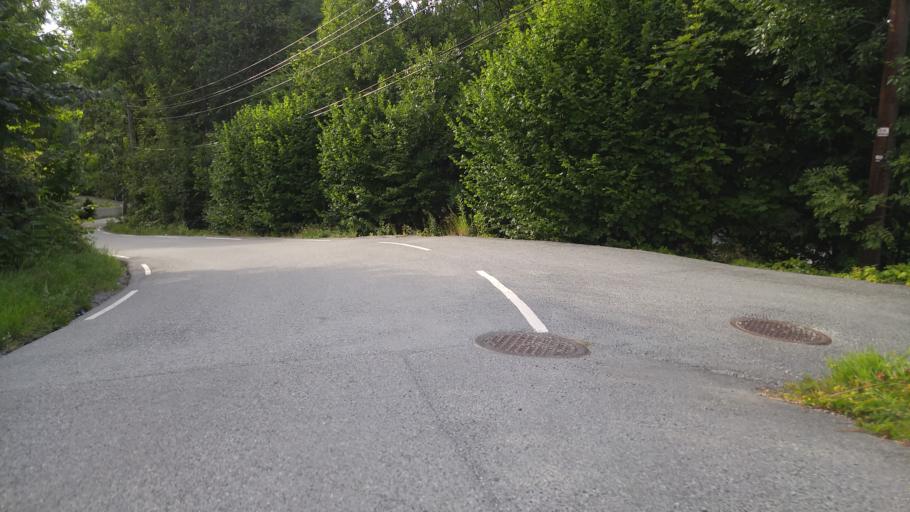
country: NO
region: Akershus
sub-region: Asker
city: Billingstad
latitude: 59.8484
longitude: 10.4929
